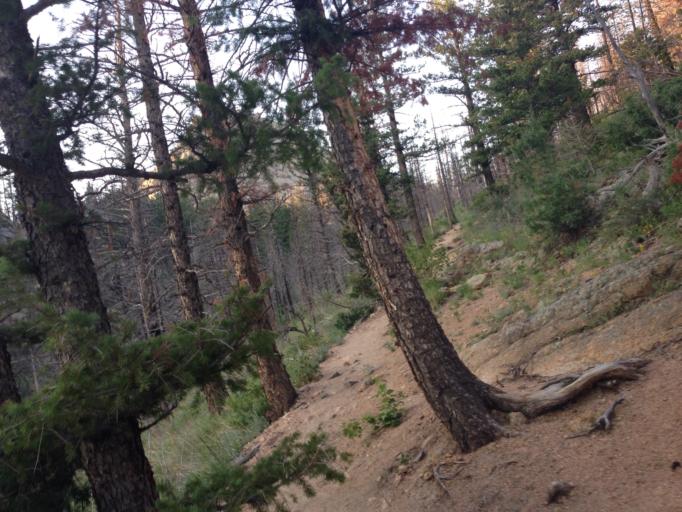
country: US
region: Colorado
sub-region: Larimer County
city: Laporte
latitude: 40.7094
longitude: -105.2945
